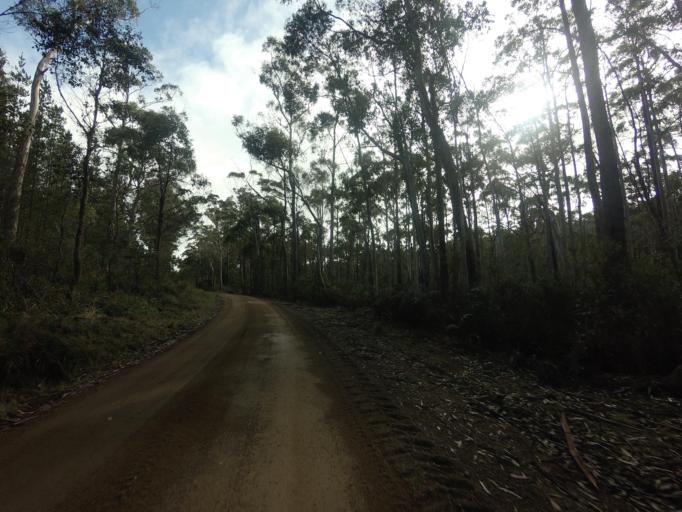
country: AU
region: Tasmania
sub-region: Derwent Valley
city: New Norfolk
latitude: -42.7644
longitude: 146.8983
